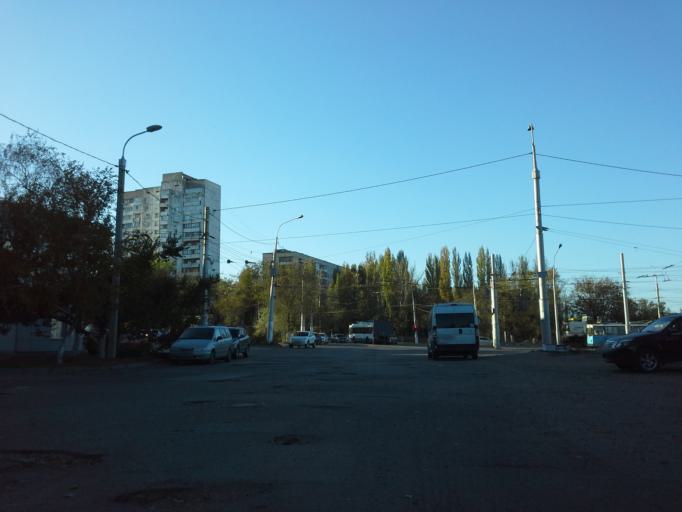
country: RU
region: Volgograd
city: Vodstroy
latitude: 48.8229
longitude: 44.6423
